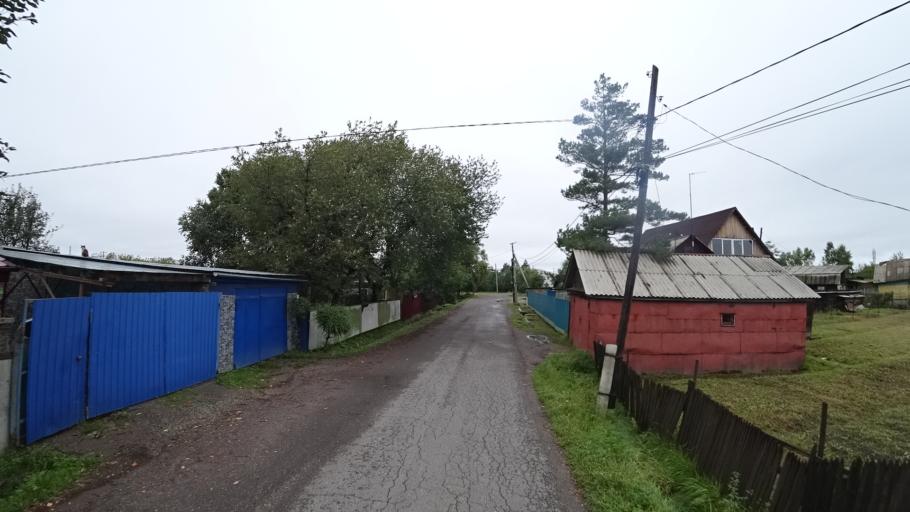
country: RU
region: Primorskiy
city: Monastyrishche
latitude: 44.2030
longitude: 132.4407
